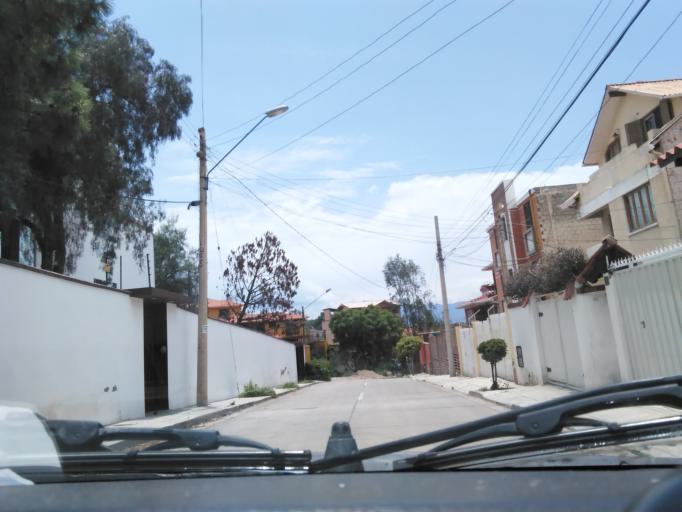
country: BO
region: Cochabamba
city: Cochabamba
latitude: -17.3713
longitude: -66.1363
